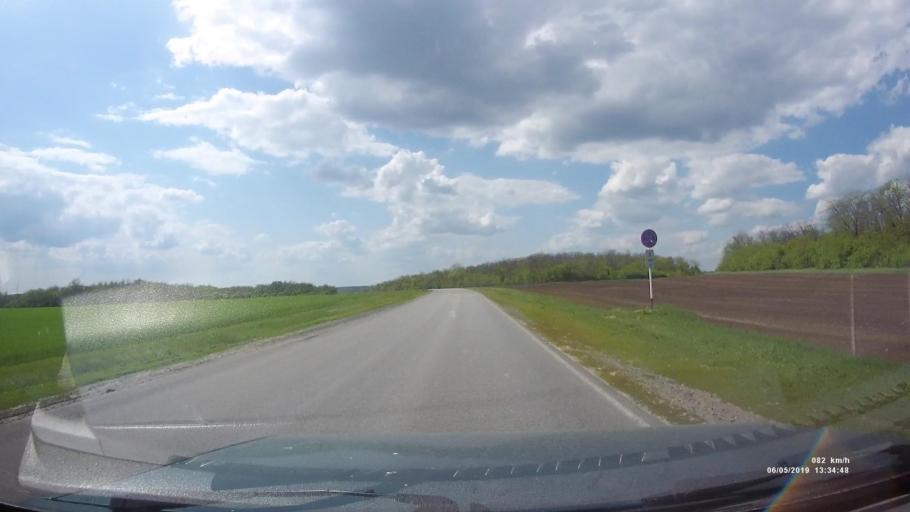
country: RU
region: Rostov
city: Ust'-Donetskiy
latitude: 47.6938
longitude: 40.7572
